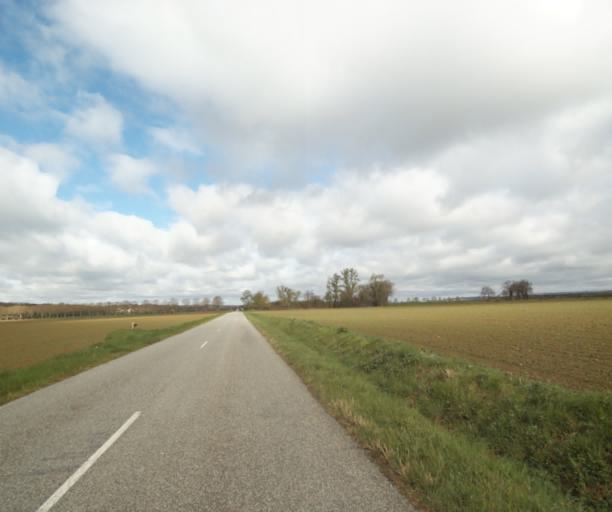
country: FR
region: Midi-Pyrenees
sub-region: Departement de l'Ariege
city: Saverdun
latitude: 43.2494
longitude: 1.5535
